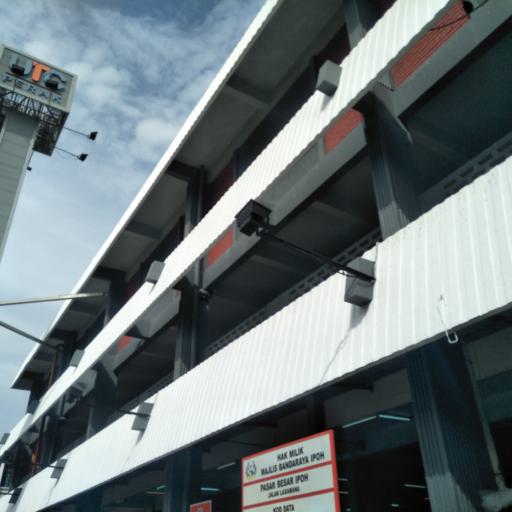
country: MY
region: Perak
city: Ipoh
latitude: 4.5957
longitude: 101.0828
